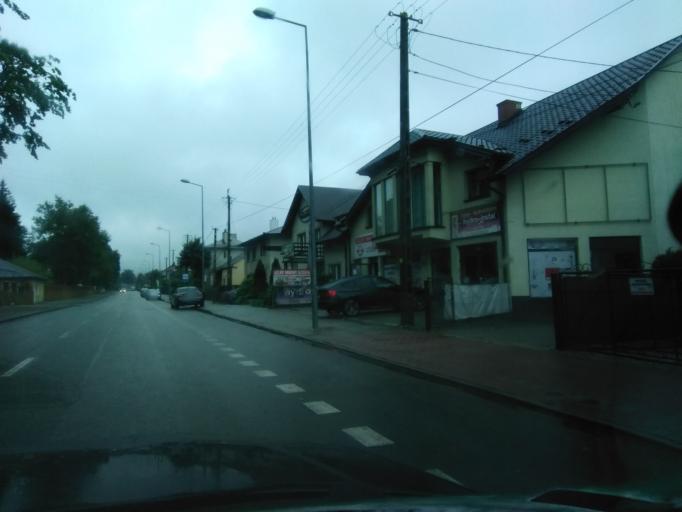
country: PL
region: Subcarpathian Voivodeship
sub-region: Powiat debicki
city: Debica
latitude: 50.0606
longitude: 21.4064
